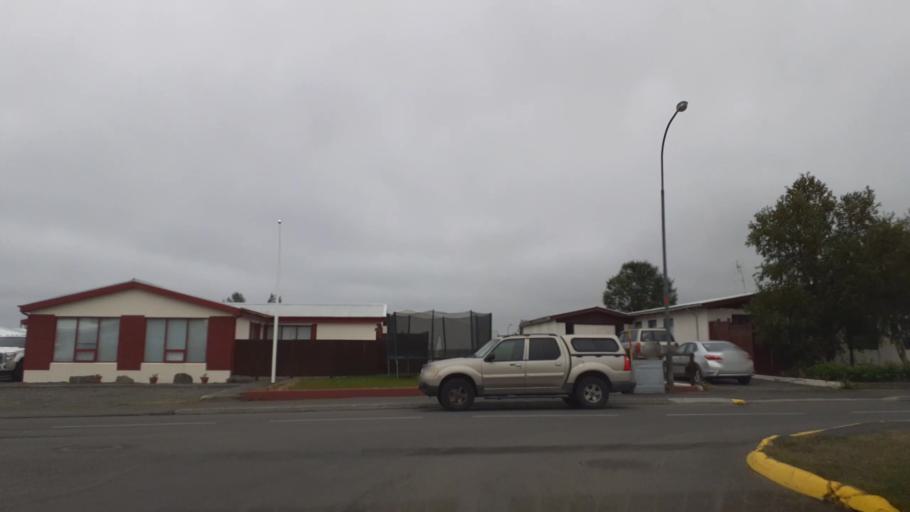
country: IS
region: Northeast
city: Dalvik
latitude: 65.9708
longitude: -18.5396
